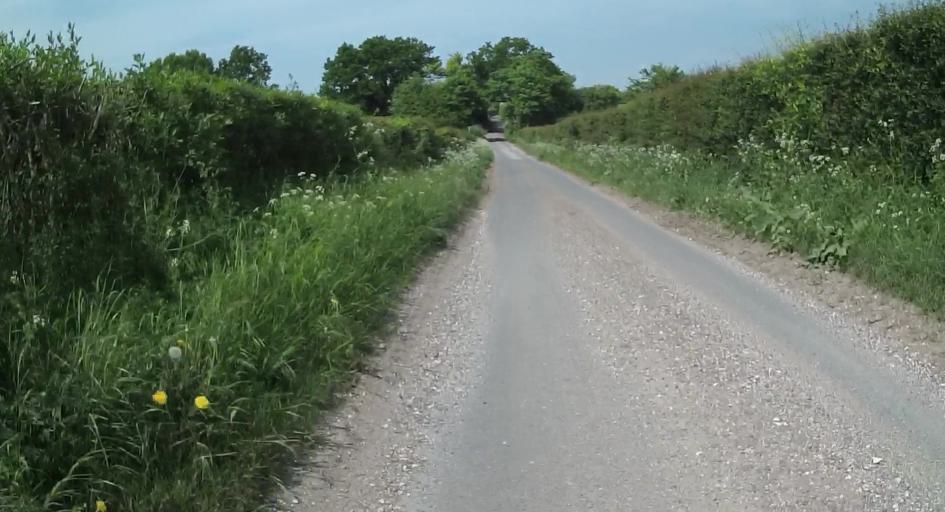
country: GB
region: England
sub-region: Hampshire
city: Overton
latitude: 51.2641
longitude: -1.2330
